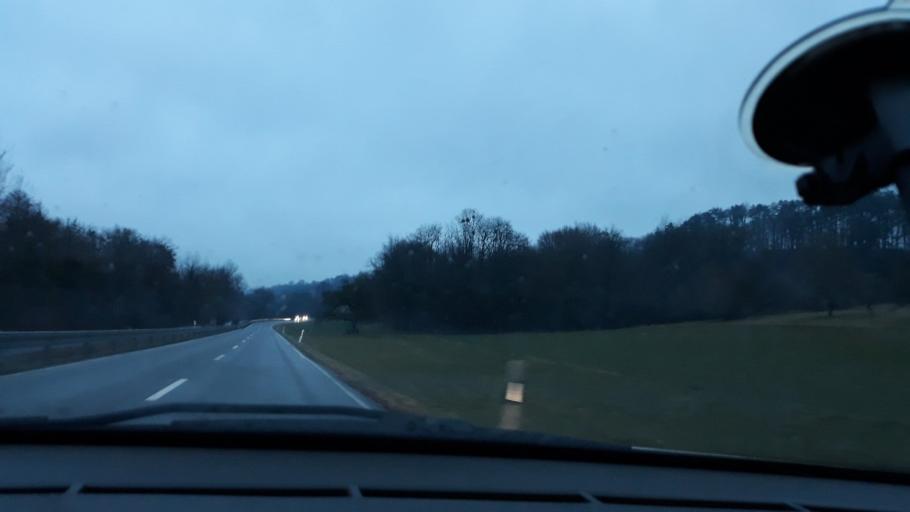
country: DE
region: Saarland
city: Gersheim
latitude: 49.1788
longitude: 7.2432
